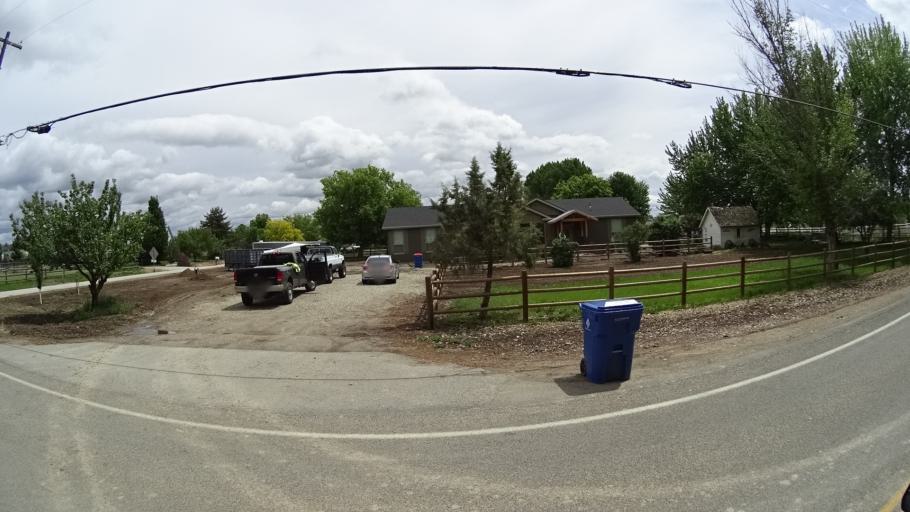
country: US
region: Idaho
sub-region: Ada County
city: Eagle
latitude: 43.7163
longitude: -116.4035
